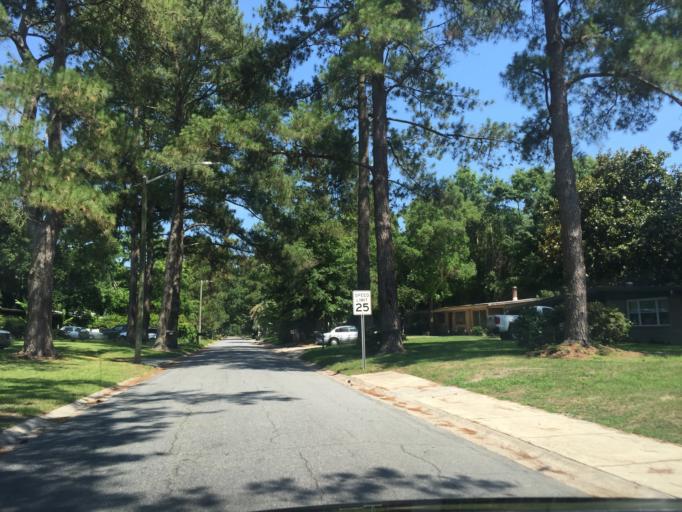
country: US
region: Georgia
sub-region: Chatham County
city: Montgomery
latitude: 31.9766
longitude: -81.1417
